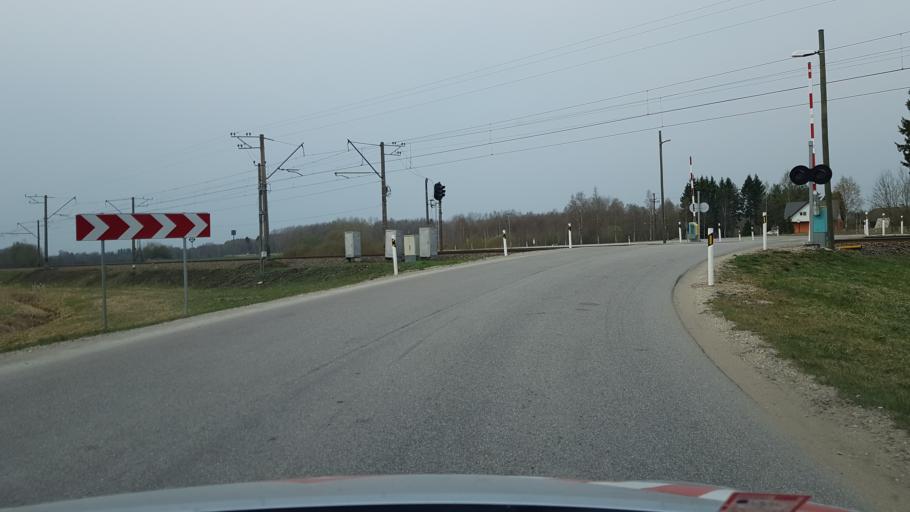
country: EE
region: Harju
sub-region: Joelaehtme vald
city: Loo
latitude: 59.3834
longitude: 25.0007
